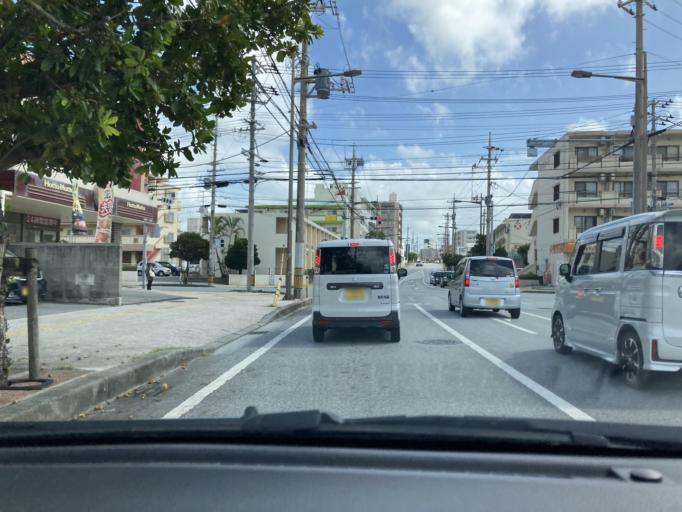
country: JP
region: Okinawa
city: Ginowan
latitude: 26.2733
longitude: 127.7300
